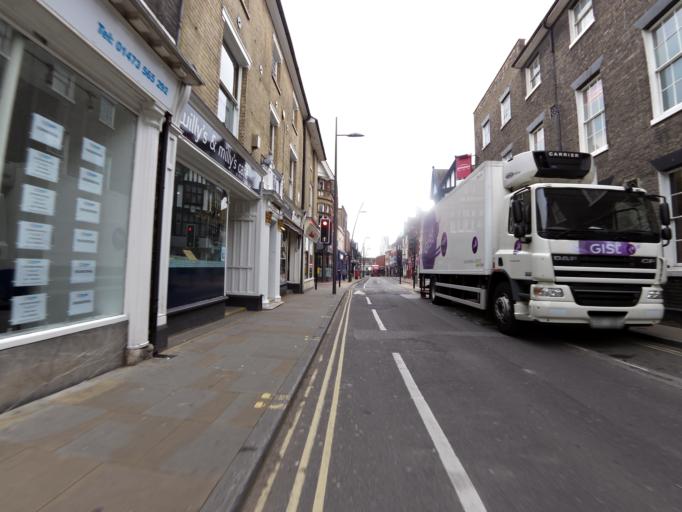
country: GB
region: England
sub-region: Suffolk
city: Ipswich
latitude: 52.0579
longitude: 1.1564
